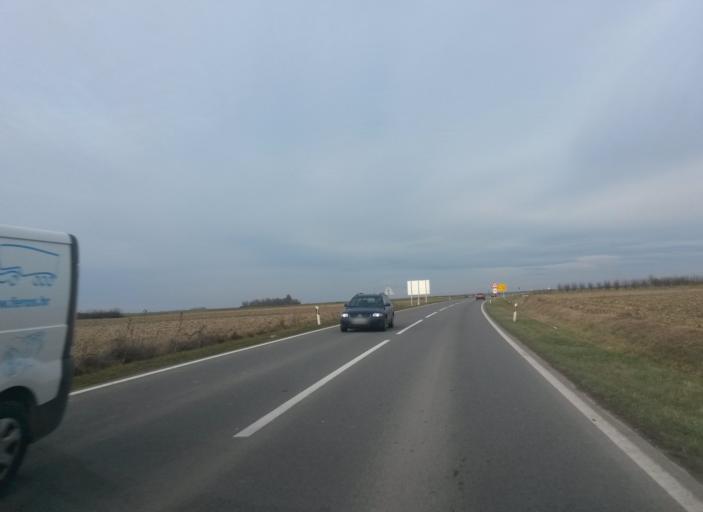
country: HR
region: Osjecko-Baranjska
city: Cepin
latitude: 45.5182
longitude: 18.5369
